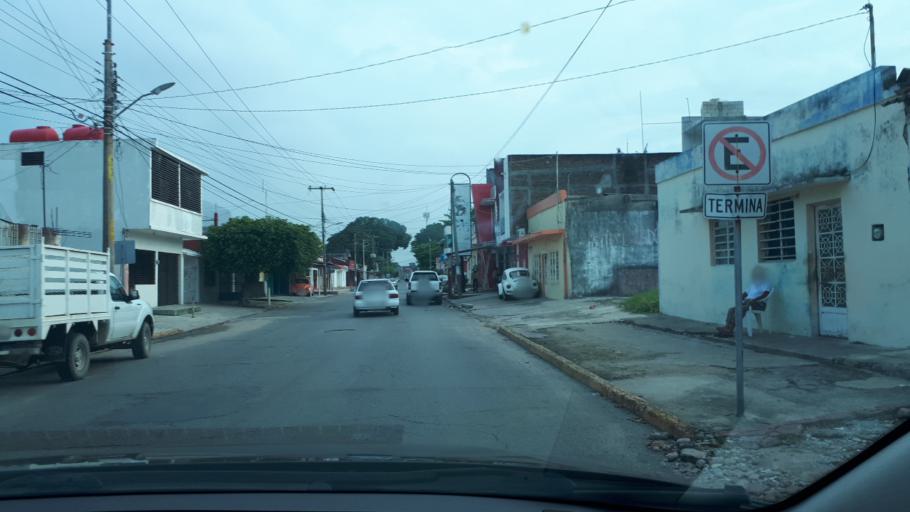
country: MX
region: Tabasco
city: Comalcalco
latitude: 18.2747
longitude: -93.2232
